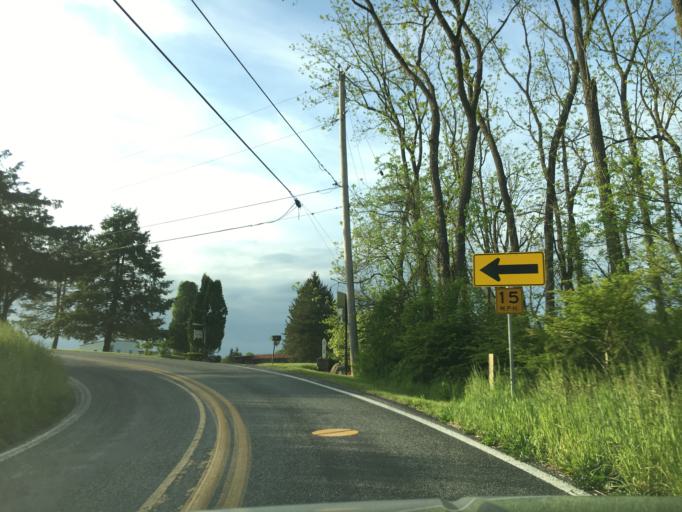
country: US
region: Pennsylvania
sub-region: Berks County
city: Fleetwood
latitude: 40.4426
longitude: -75.7721
